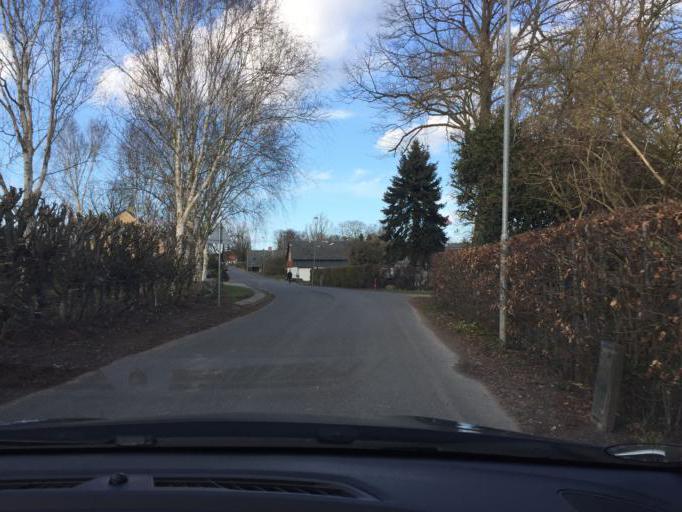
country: DK
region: South Denmark
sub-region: Nyborg Kommune
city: Ullerslev
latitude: 55.3527
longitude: 10.7223
